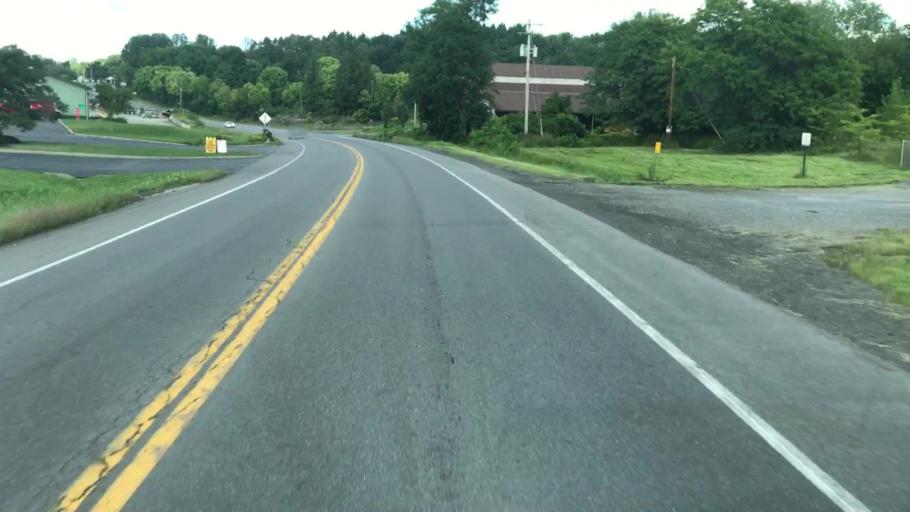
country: US
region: New York
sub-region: Onondaga County
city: Marcellus
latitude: 42.9770
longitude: -76.3315
